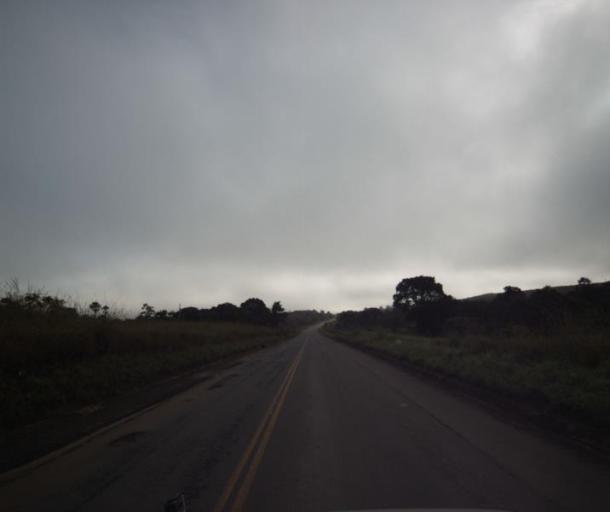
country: BR
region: Goias
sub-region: Pirenopolis
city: Pirenopolis
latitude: -15.7636
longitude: -48.7576
